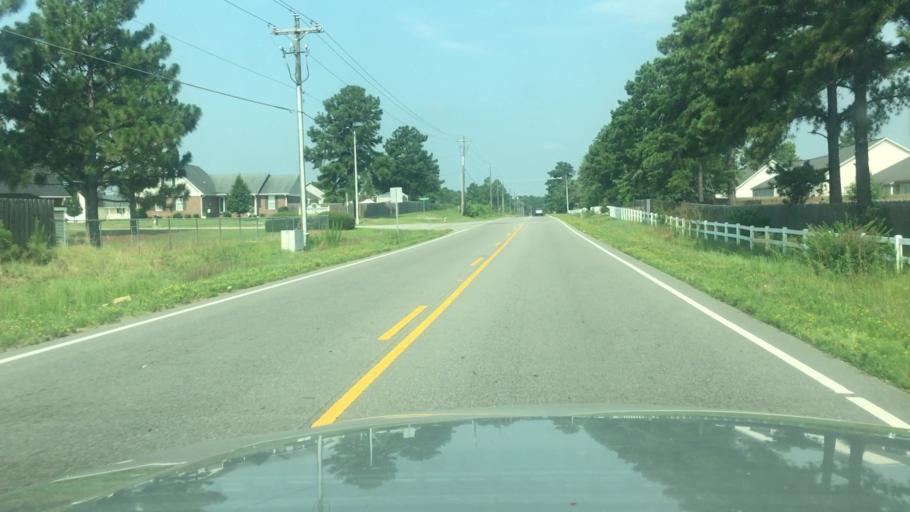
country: US
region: North Carolina
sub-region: Cumberland County
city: Hope Mills
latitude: 34.9999
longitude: -78.9446
